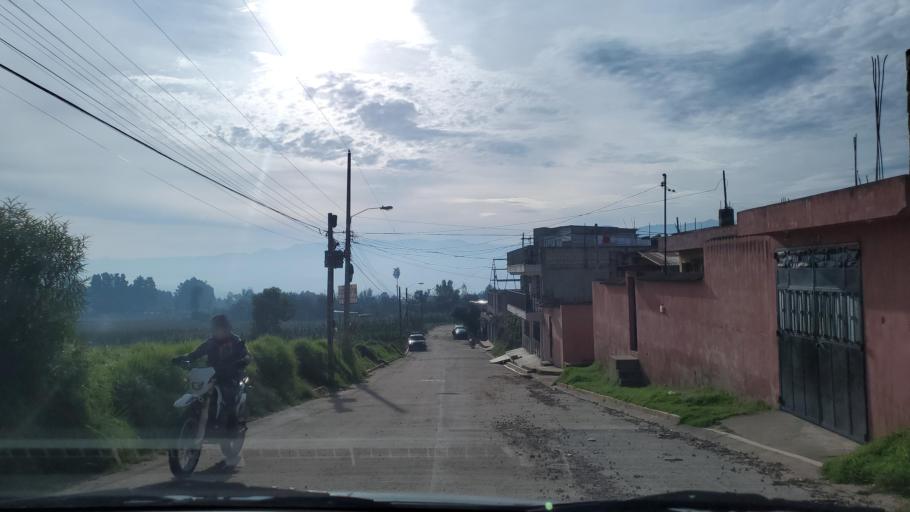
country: GT
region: Quetzaltenango
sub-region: Municipio de La Esperanza
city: La Esperanza
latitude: 14.8427
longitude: -91.5481
